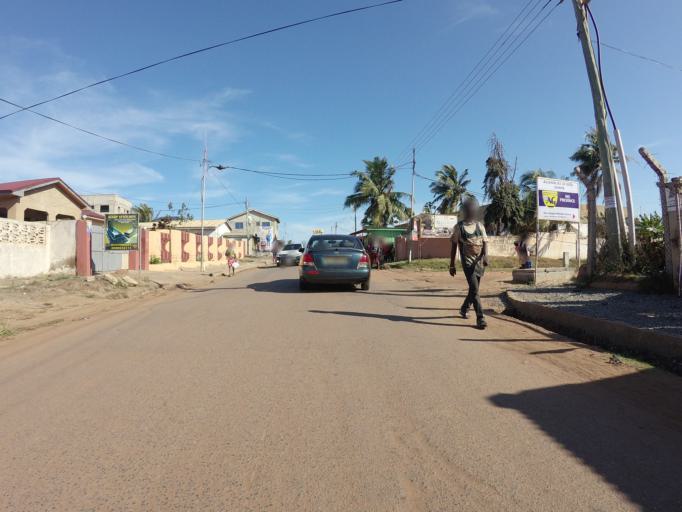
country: GH
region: Greater Accra
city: Nungua
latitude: 5.5913
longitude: -0.0827
